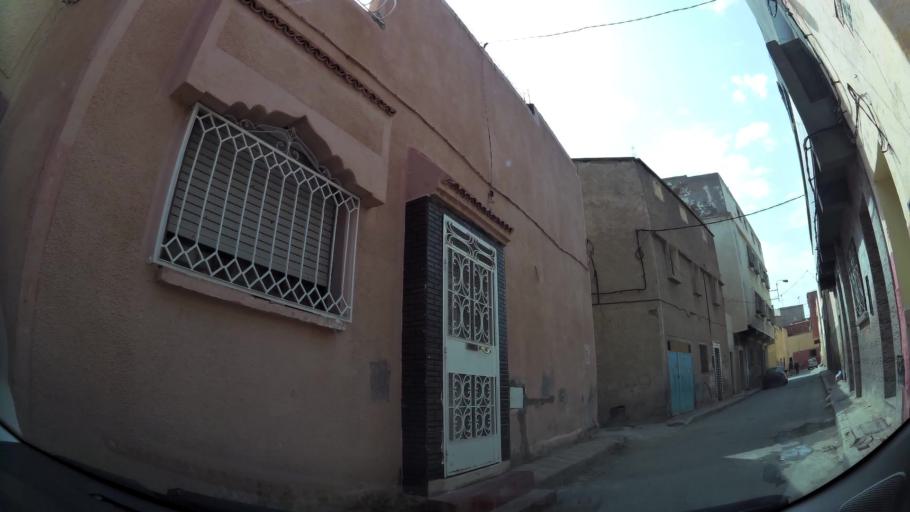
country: MA
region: Oriental
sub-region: Oujda-Angad
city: Oujda
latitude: 34.6831
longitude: -1.9068
